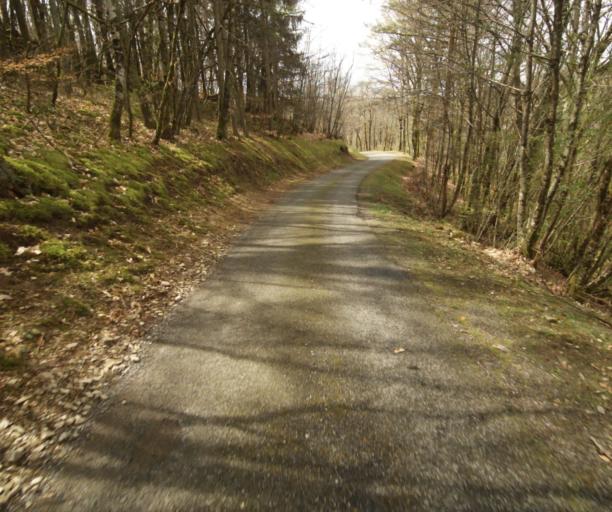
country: FR
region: Limousin
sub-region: Departement de la Correze
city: Sainte-Fortunade
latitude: 45.1970
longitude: 1.8809
